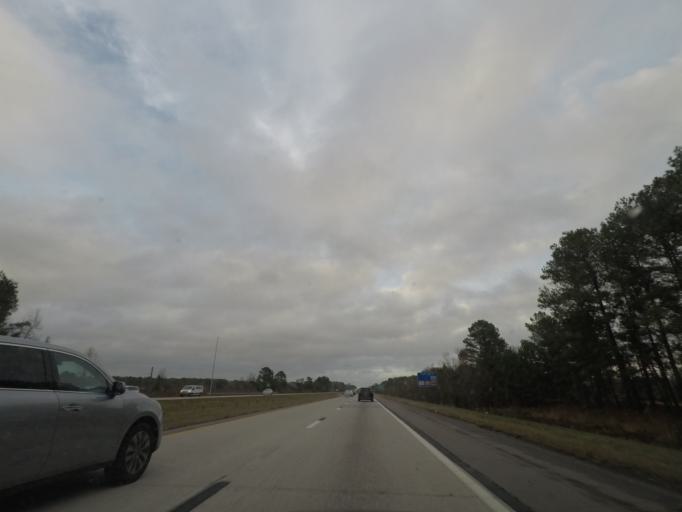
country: US
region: South Carolina
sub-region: Dorchester County
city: Saint George
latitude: 33.1794
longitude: -80.6128
